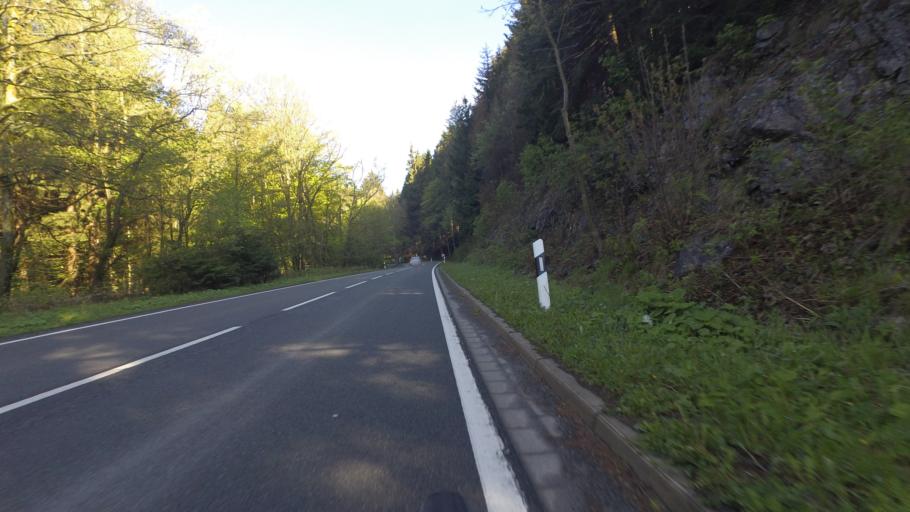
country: DE
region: Saxony-Anhalt
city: Benneckenstein
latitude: 51.7586
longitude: 10.7015
